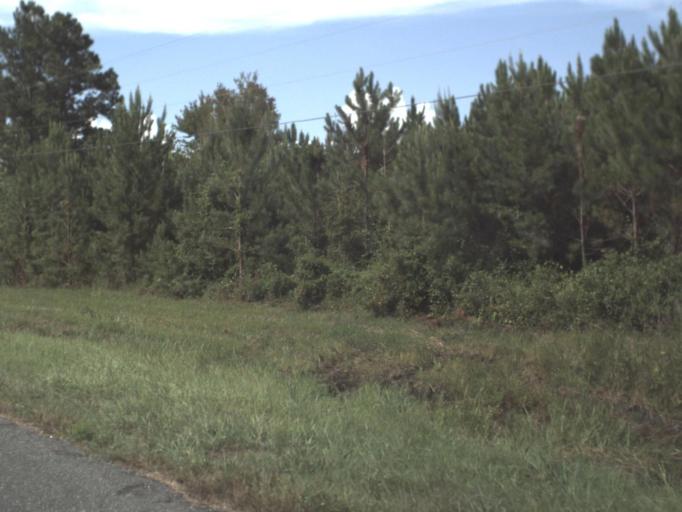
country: US
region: Florida
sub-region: Taylor County
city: Perry
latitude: 30.2300
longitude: -83.6170
